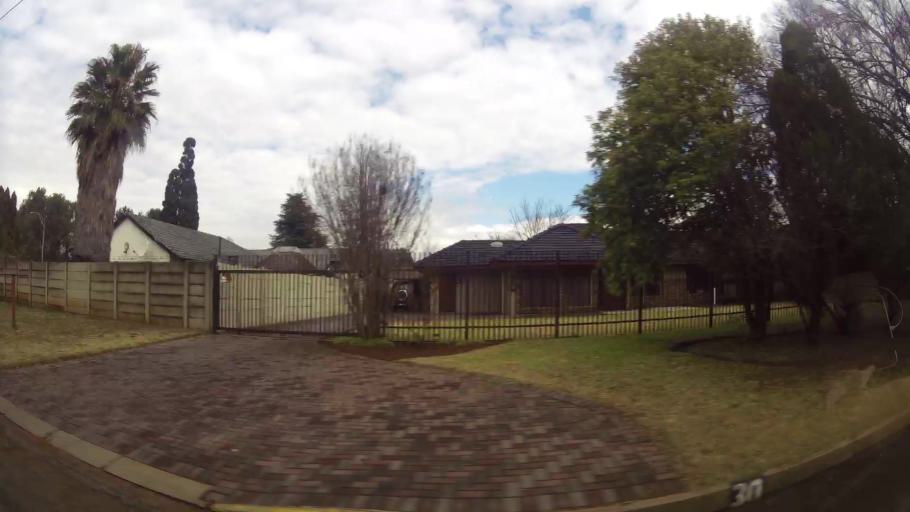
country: ZA
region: Gauteng
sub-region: Sedibeng District Municipality
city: Vereeniging
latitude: -26.6416
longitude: 27.9801
